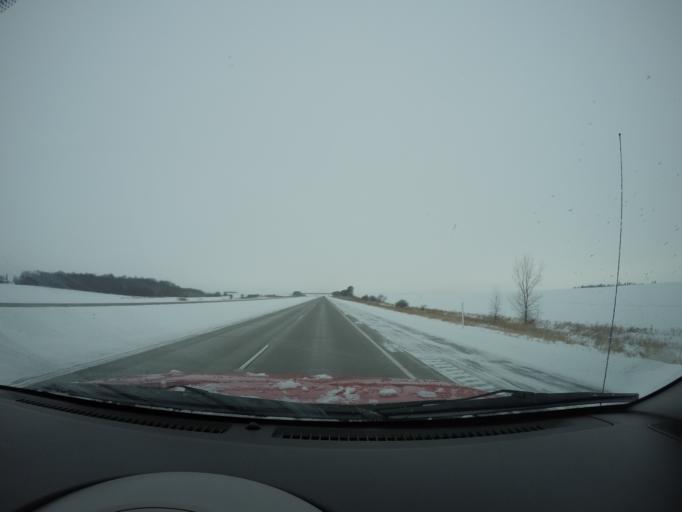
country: US
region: Minnesota
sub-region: Olmsted County
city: Eyota
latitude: 43.9553
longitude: -92.1700
